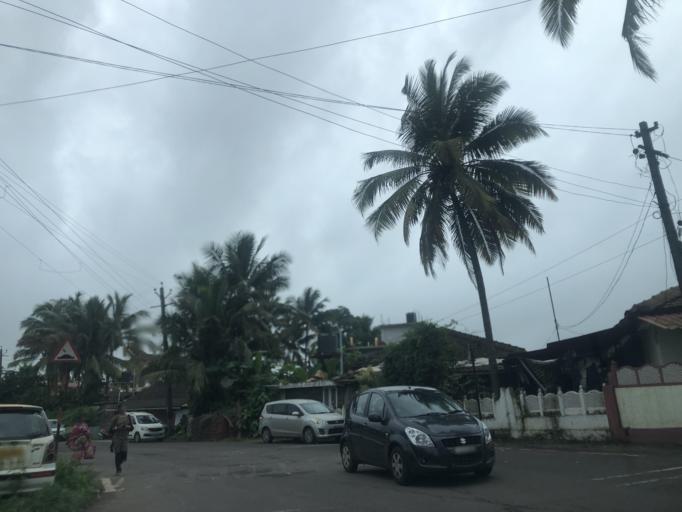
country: IN
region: Goa
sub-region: North Goa
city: Serula
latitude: 15.5480
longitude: 73.8252
